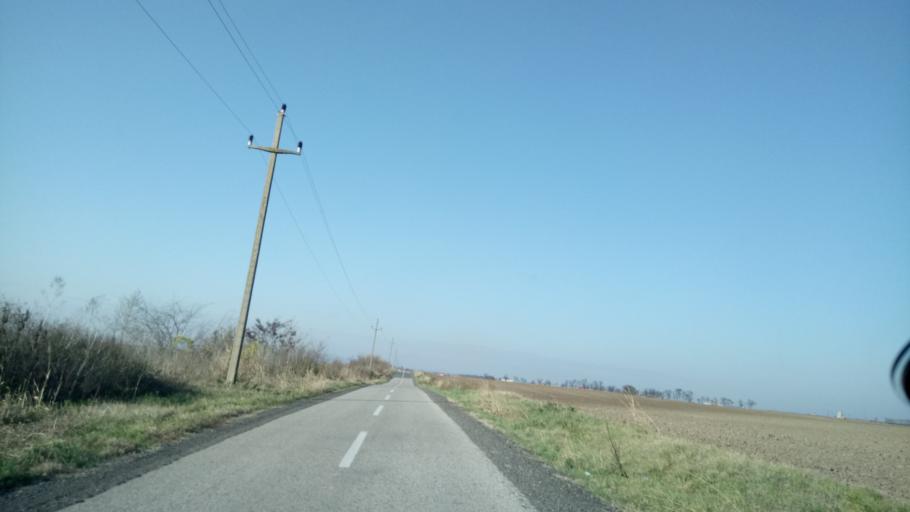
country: RS
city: Ljukovo
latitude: 45.0310
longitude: 20.0469
